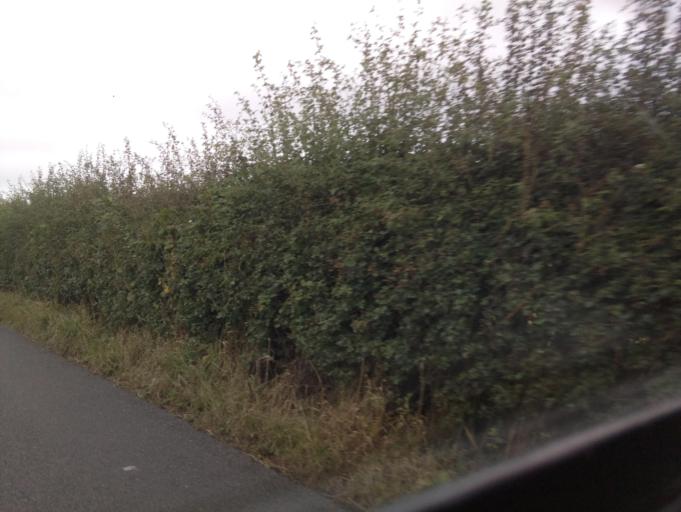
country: GB
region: England
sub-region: Leicestershire
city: Ashby de la Zouch
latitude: 52.7718
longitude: -1.5044
